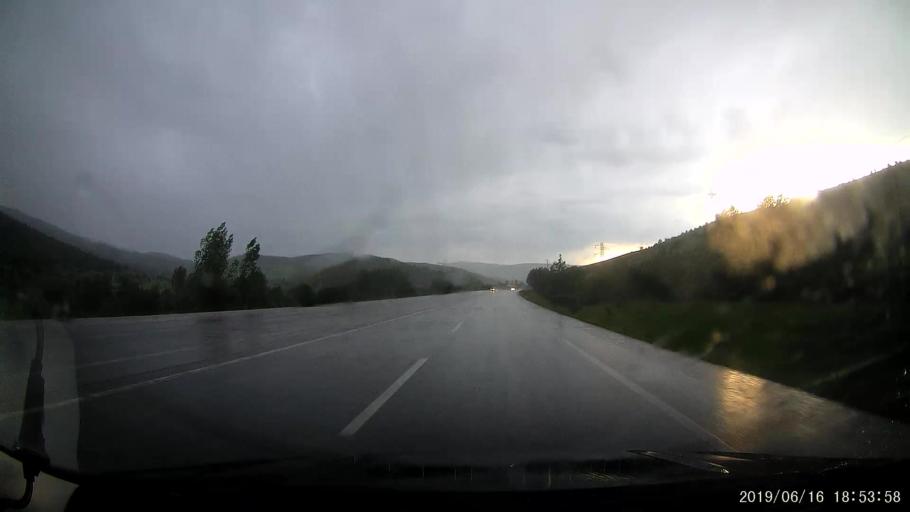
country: TR
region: Erzincan
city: Catalcam
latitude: 39.8965
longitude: 38.8645
